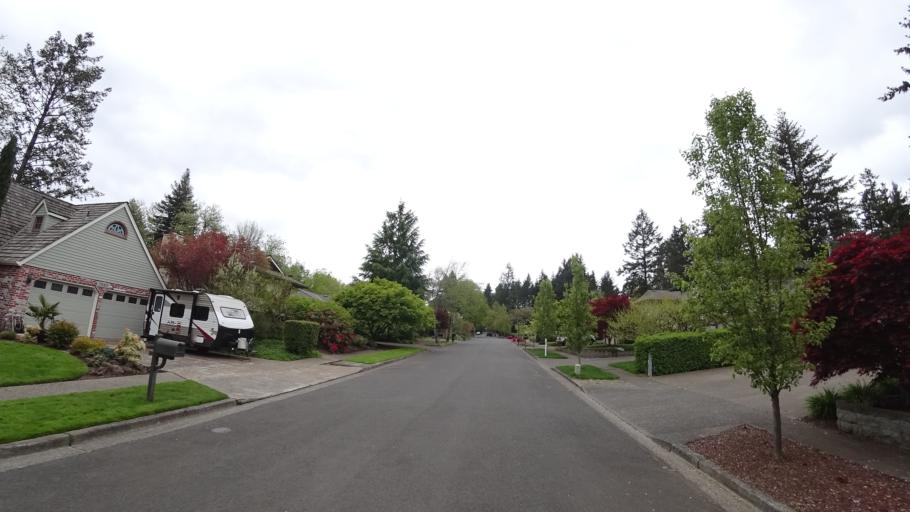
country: US
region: Oregon
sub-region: Washington County
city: Beaverton
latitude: 45.4644
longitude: -122.8313
